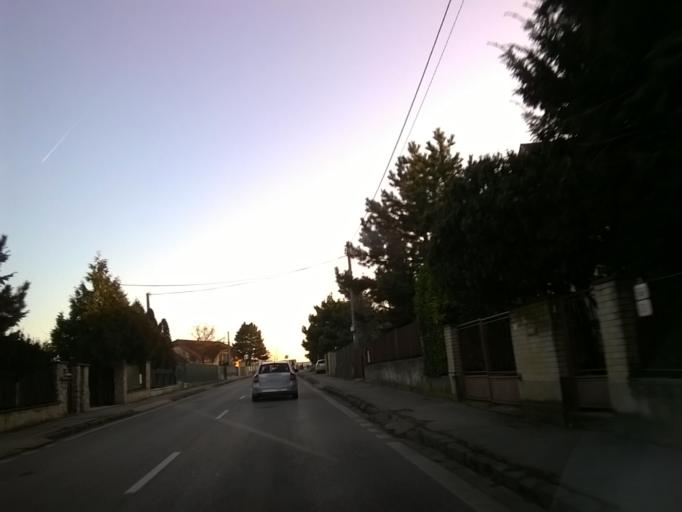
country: SK
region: Nitriansky
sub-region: Okres Nitra
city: Nitra
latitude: 48.2903
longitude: 18.0726
